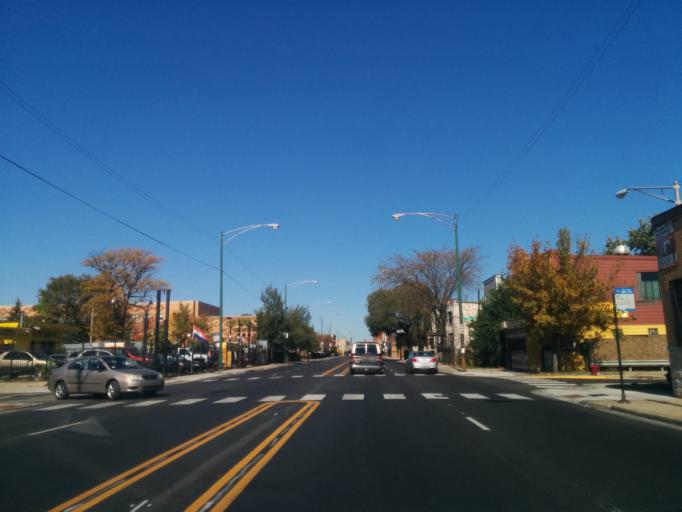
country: US
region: Illinois
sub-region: Cook County
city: Oak Park
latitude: 41.8966
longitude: -87.7458
